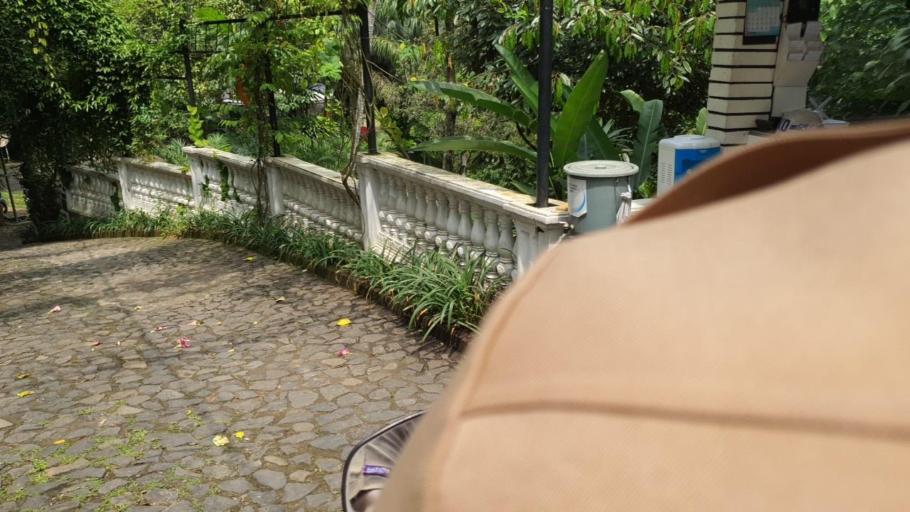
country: ID
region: West Java
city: Caringin
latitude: -6.6526
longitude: 106.8751
